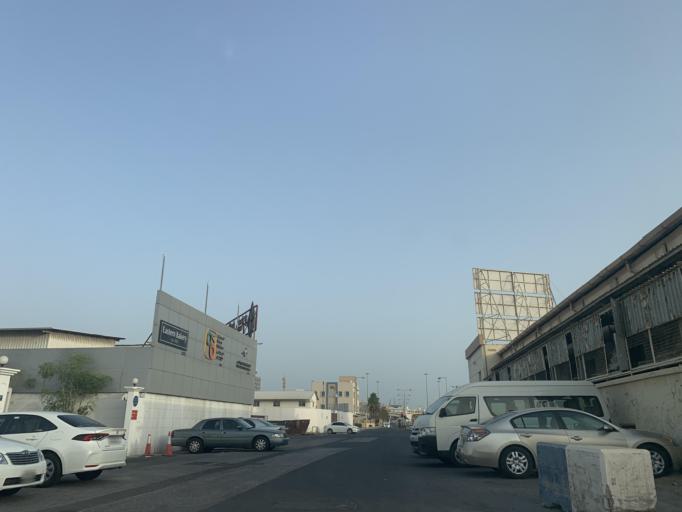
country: BH
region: Manama
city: Manama
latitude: 26.1994
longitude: 50.6043
